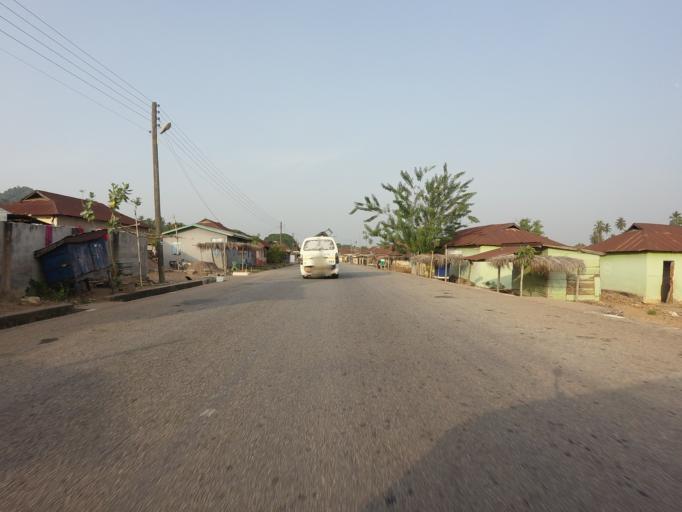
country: GH
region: Volta
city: Ho
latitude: 6.5688
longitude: 0.3040
